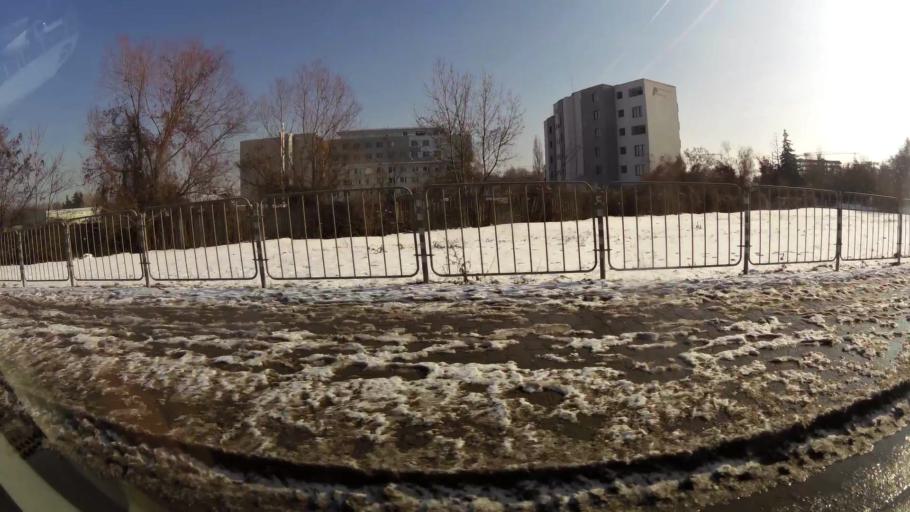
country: BG
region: Sofia-Capital
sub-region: Stolichna Obshtina
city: Sofia
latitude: 42.6612
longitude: 23.3205
